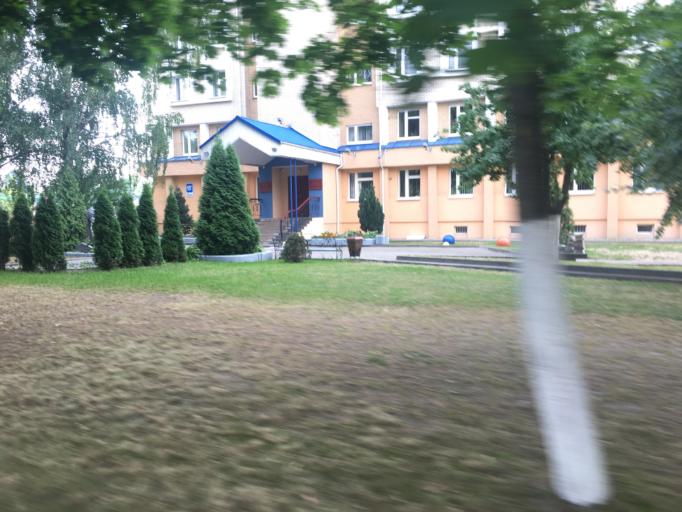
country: BY
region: Grodnenskaya
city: Hrodna
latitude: 53.6596
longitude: 23.8301
